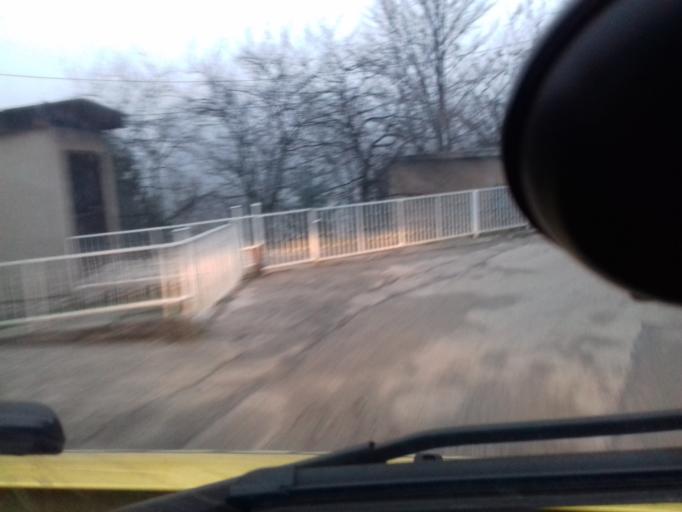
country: BA
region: Federation of Bosnia and Herzegovina
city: Zenica
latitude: 44.1987
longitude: 17.8959
